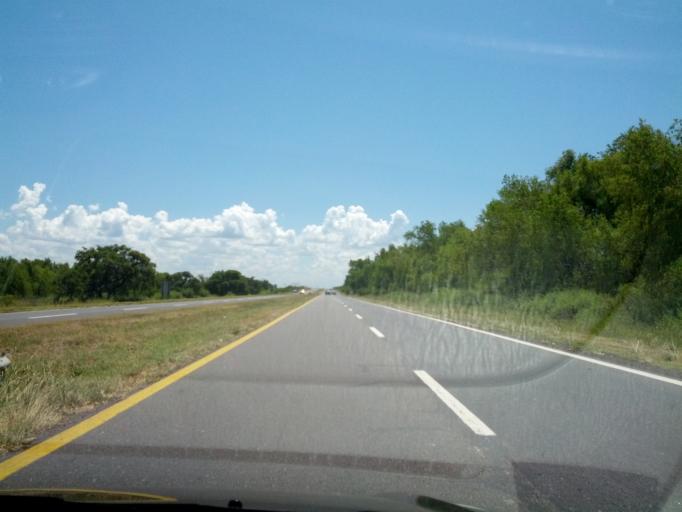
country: AR
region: Entre Rios
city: Villa Paranacito
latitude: -33.7406
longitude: -58.8555
